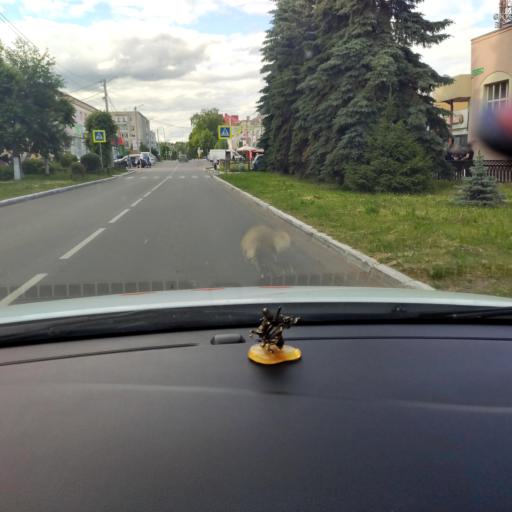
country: RU
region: Tatarstan
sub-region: Zelenodol'skiy Rayon
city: Zelenodolsk
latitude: 55.8494
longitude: 48.4984
